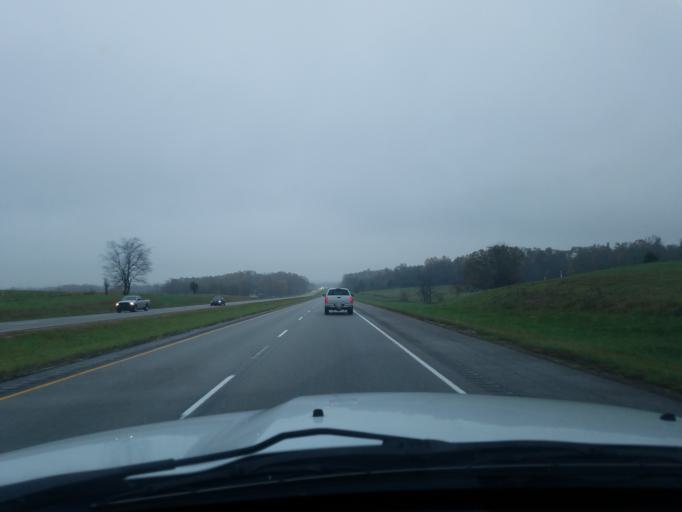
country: US
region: Kentucky
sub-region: Hardin County
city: Elizabethtown
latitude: 37.6273
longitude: -85.8192
